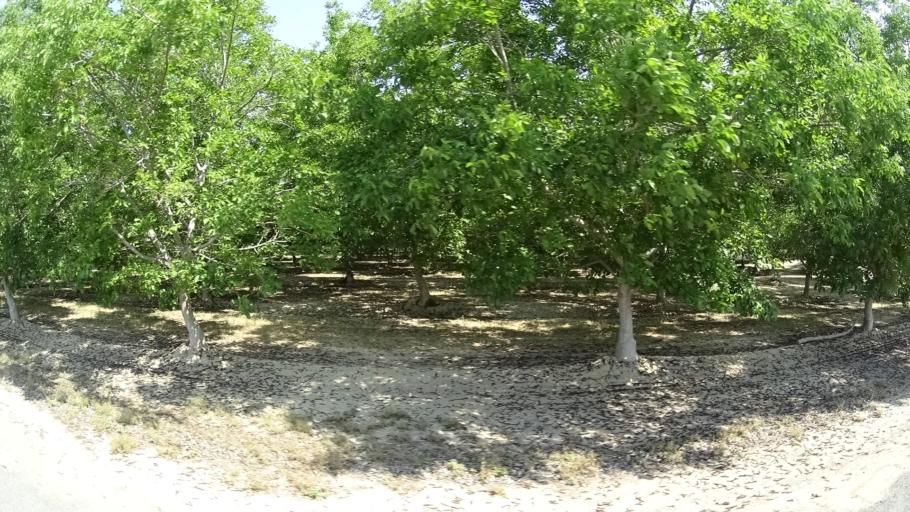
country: US
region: California
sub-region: Fresno County
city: Laton
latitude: 36.3948
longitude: -119.7649
